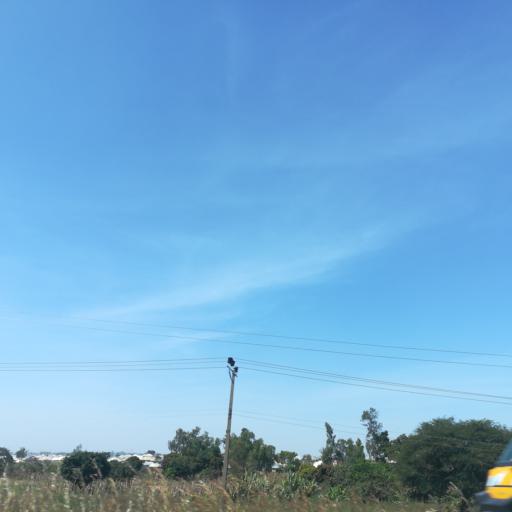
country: NG
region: Plateau
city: Bukuru
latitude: 9.7827
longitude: 8.8833
